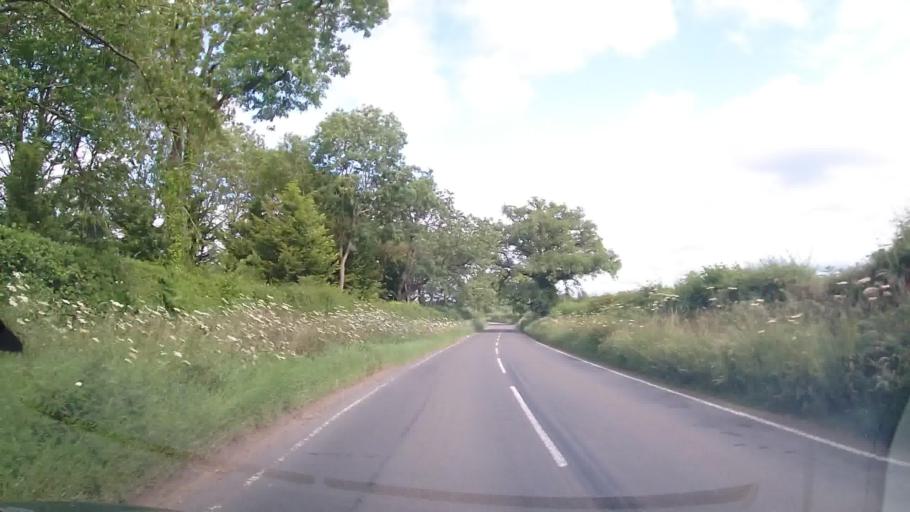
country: GB
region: England
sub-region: Shropshire
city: Great Ness
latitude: 52.7971
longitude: -2.9245
